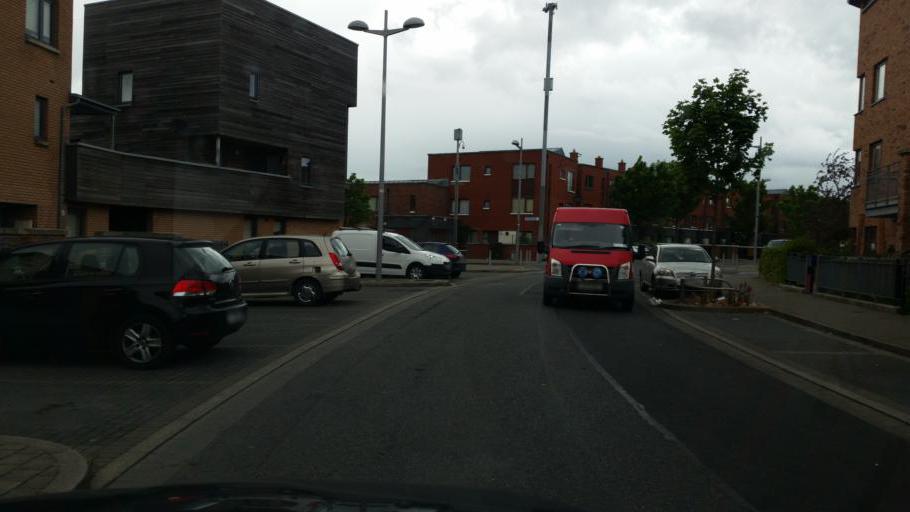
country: IE
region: Leinster
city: Ballymun
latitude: 53.3965
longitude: -6.2750
